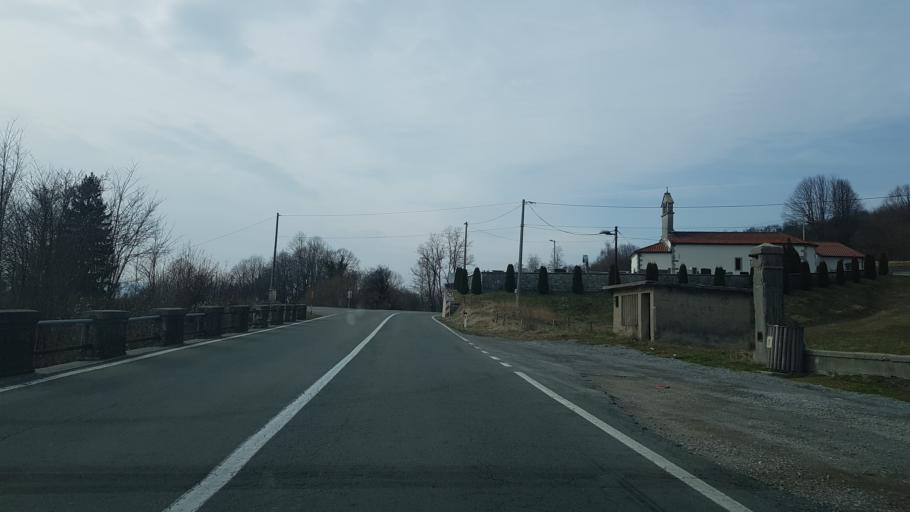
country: SI
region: Ilirska Bistrica
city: Ilirska Bistrica
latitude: 45.4965
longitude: 14.1914
